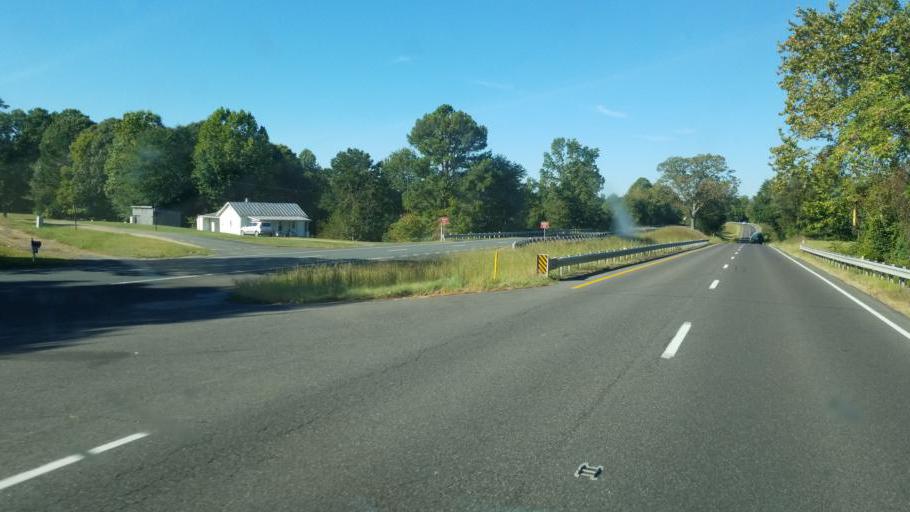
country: US
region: Virginia
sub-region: Madison County
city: Brightwood
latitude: 38.4259
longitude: -78.1796
